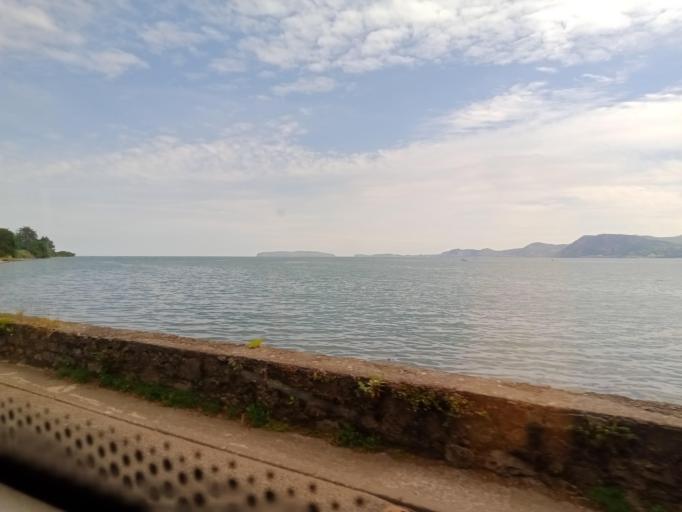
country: GB
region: Wales
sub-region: Anglesey
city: Llangoed
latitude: 53.2744
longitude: -4.0865
